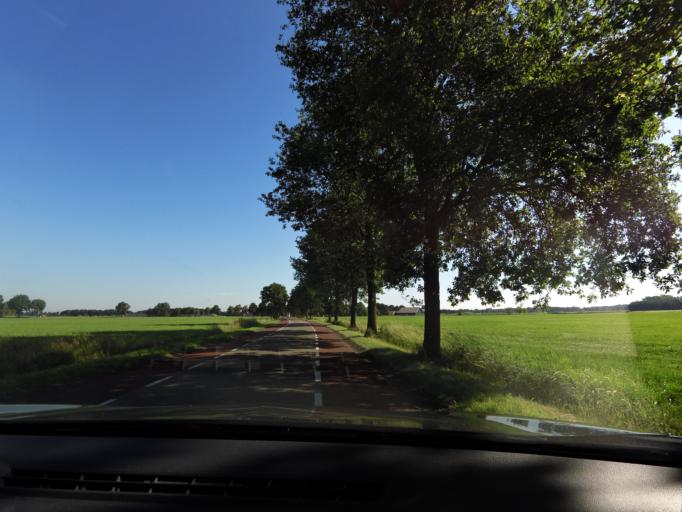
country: NL
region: Overijssel
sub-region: Gemeente Raalte
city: Raalte
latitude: 52.3489
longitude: 6.3590
